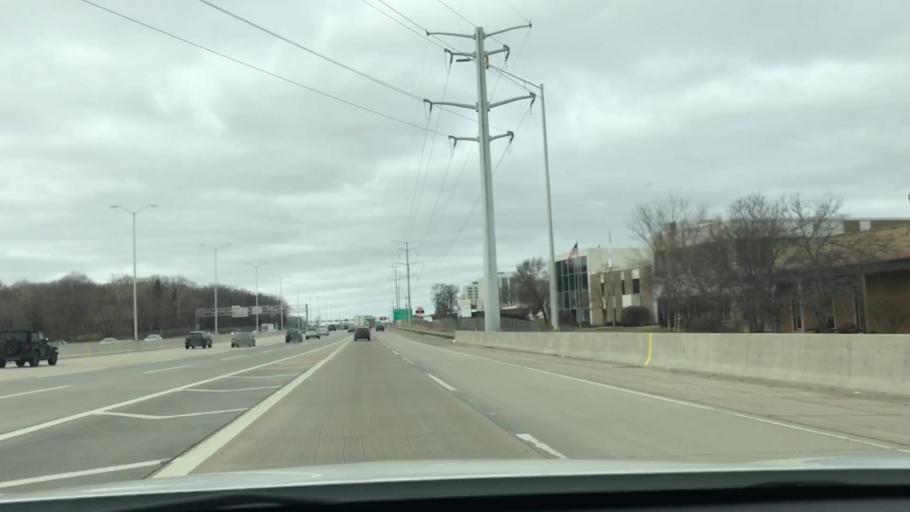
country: US
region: Illinois
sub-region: Cook County
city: Arlington Heights
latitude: 42.0444
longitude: -87.9908
